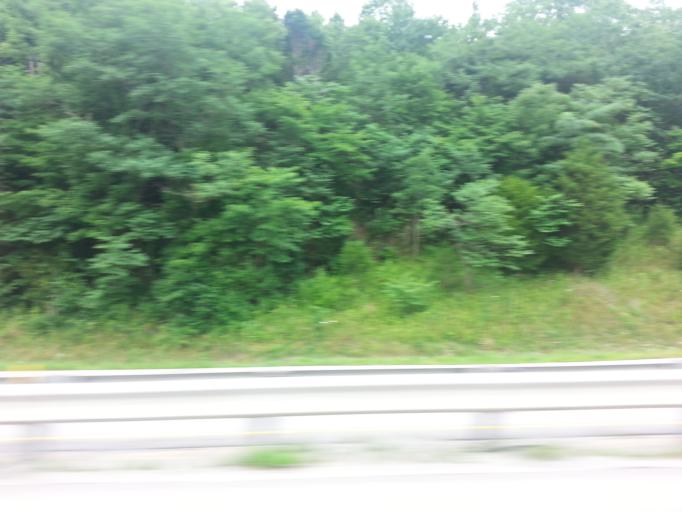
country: US
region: Ohio
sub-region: Brown County
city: Ripley
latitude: 38.7566
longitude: -83.8280
